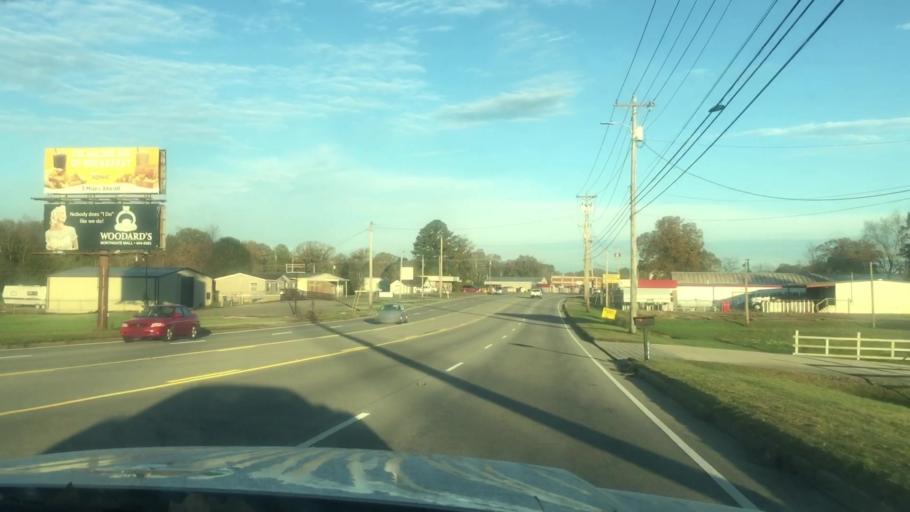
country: US
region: Tennessee
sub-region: Coffee County
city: Tullahoma
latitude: 35.3487
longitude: -86.1990
